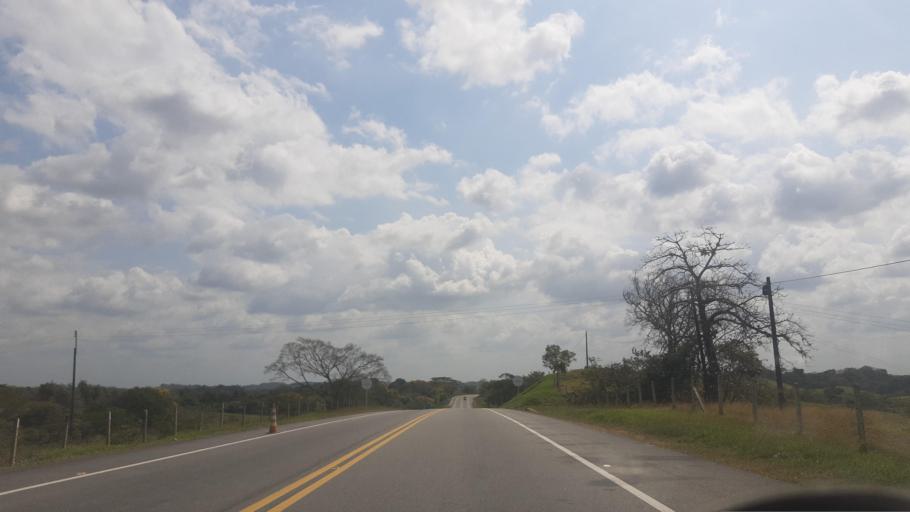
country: CO
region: Casanare
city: Monterrey
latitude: 4.8293
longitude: -72.8157
